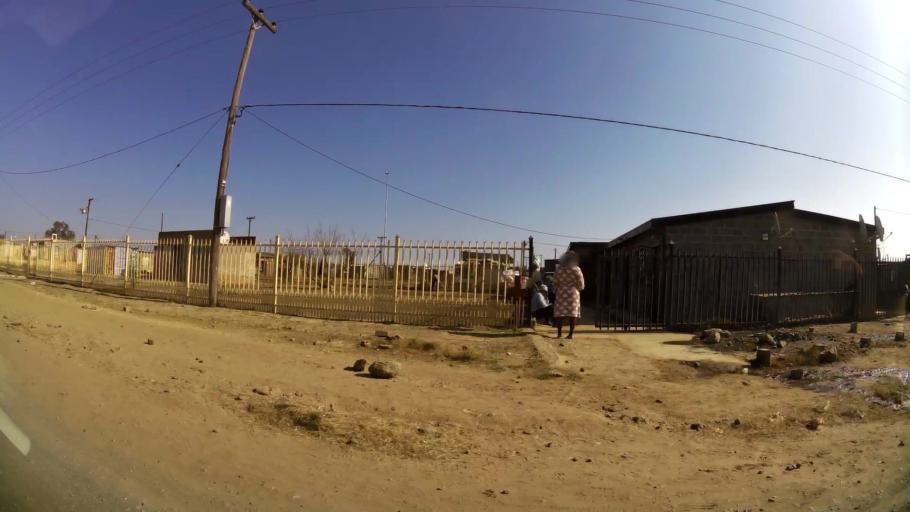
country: ZA
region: Orange Free State
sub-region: Mangaung Metropolitan Municipality
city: Bloemfontein
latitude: -29.1788
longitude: 26.2880
